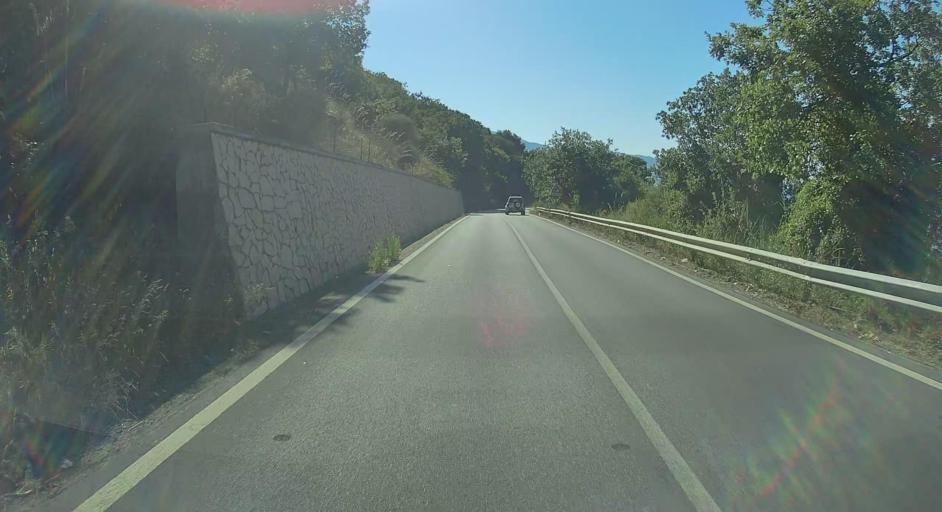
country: IT
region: Sicily
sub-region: Messina
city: Oliveri
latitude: 38.1426
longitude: 15.0274
